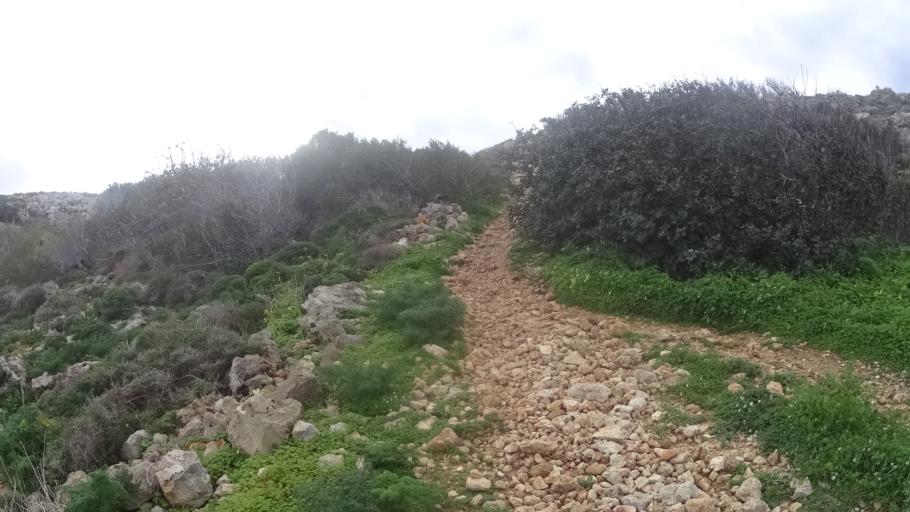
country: MT
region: Il-Mellieha
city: Mellieha
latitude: 35.9760
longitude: 14.3264
